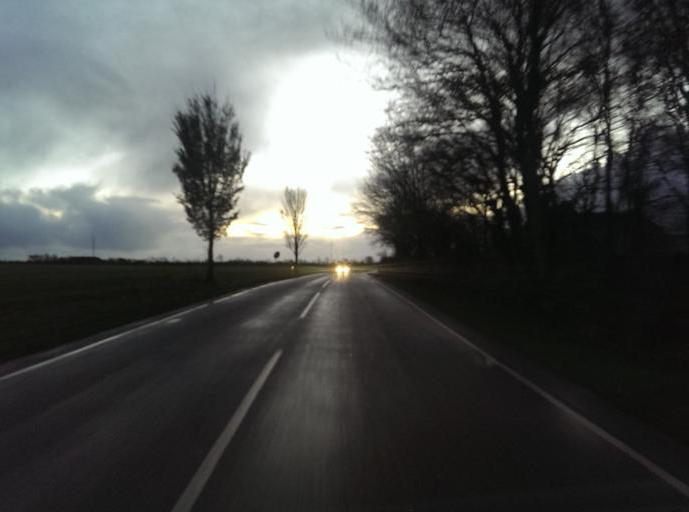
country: DK
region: South Denmark
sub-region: Esbjerg Kommune
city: Bramming
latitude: 55.4370
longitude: 8.6845
